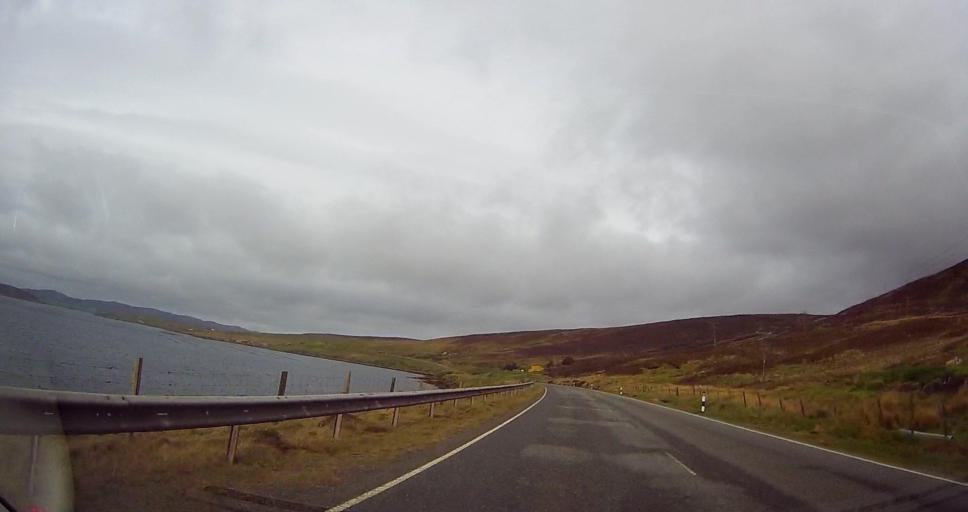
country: GB
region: Scotland
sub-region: Shetland Islands
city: Lerwick
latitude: 60.3668
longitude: -1.2916
